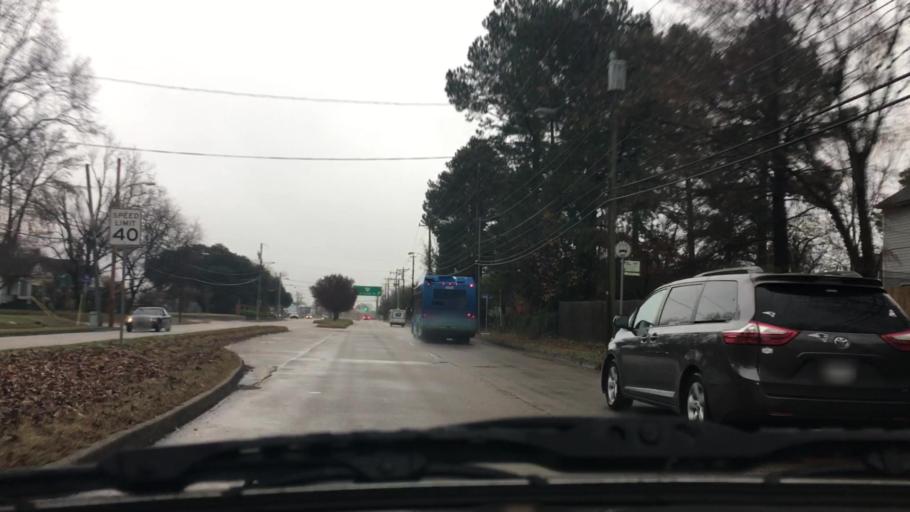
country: US
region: Virginia
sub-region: City of Norfolk
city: Norfolk
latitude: 36.9205
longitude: -76.2532
